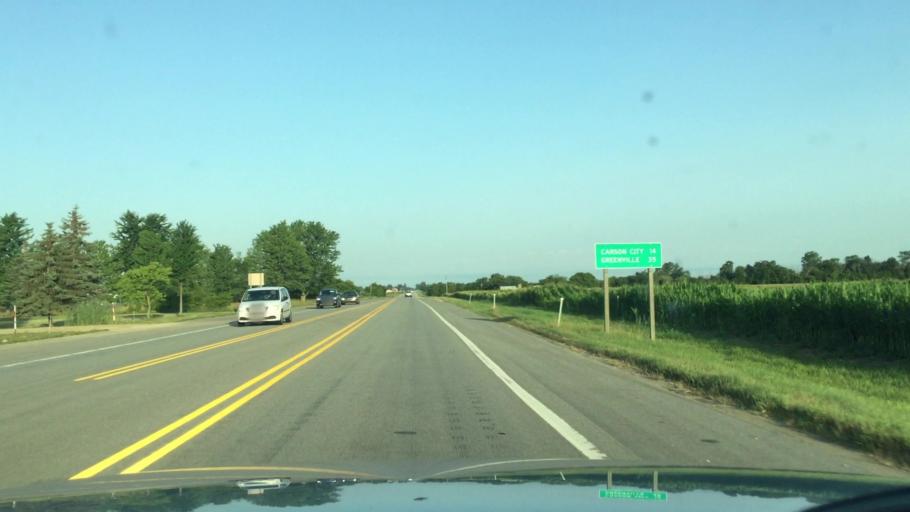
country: US
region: Michigan
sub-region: Gratiot County
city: Ithaca
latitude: 43.1761
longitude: -84.5699
